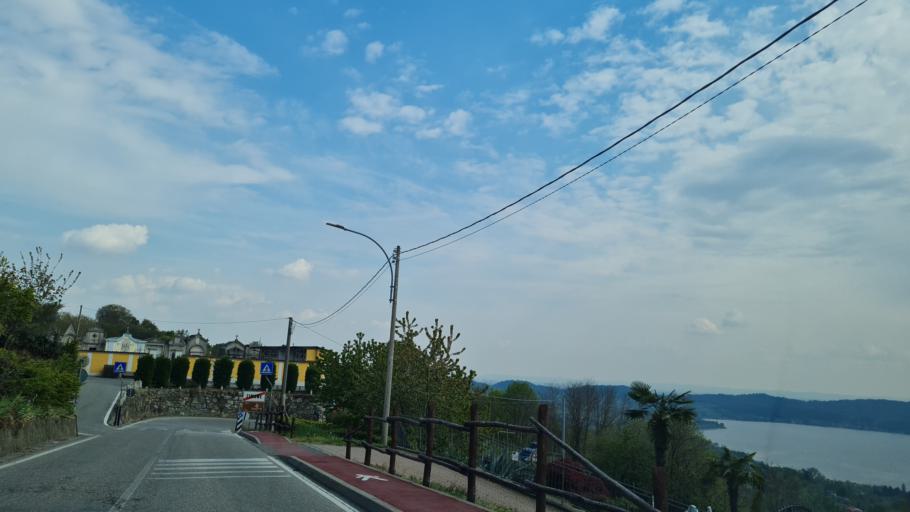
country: IT
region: Piedmont
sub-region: Provincia di Biella
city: Zimone
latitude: 45.4465
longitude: 8.0366
